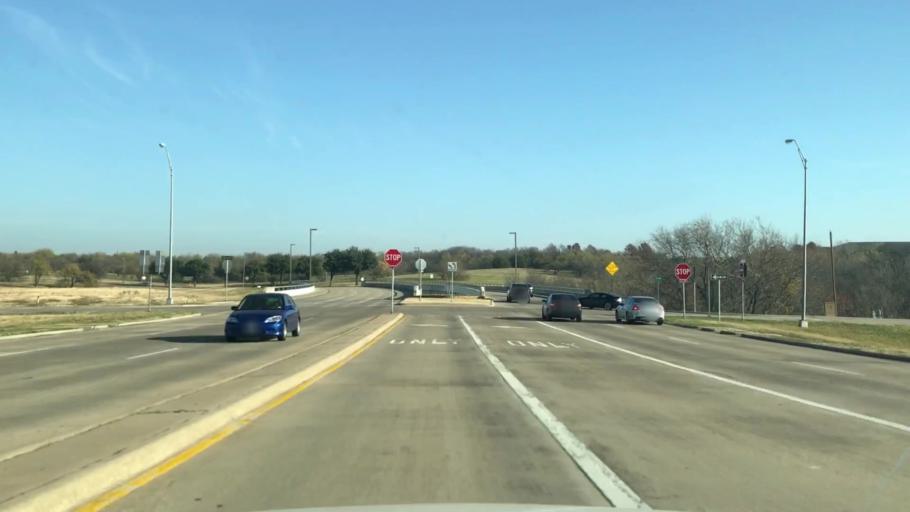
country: US
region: Texas
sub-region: Dallas County
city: Farmers Branch
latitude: 32.8879
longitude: -96.9550
